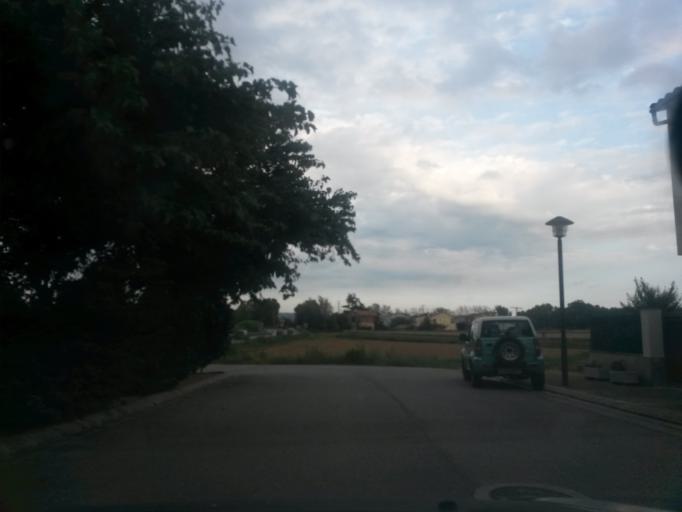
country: ES
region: Catalonia
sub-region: Provincia de Girona
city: Vilablareix
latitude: 41.9697
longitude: 2.7638
